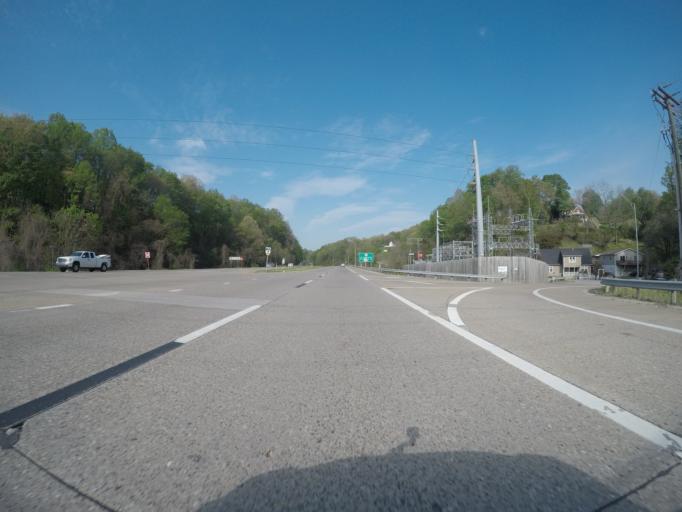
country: US
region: West Virginia
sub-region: Kanawha County
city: South Charleston
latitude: 38.3403
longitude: -81.6849
